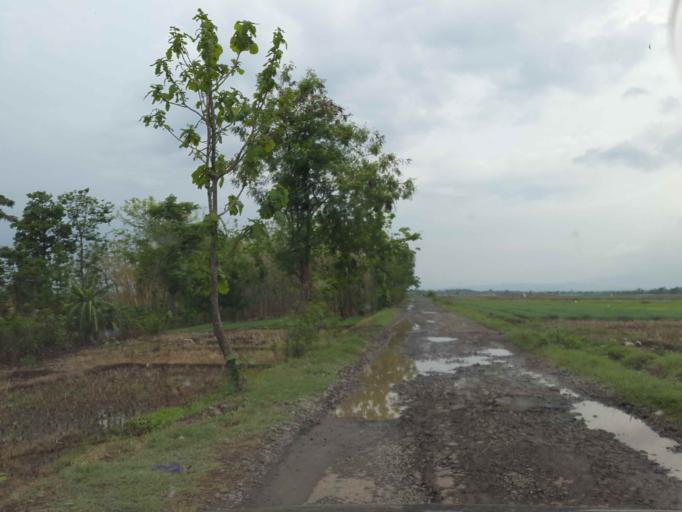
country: ID
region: Central Java
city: Ketanggungan
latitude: -6.9491
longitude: 108.9452
